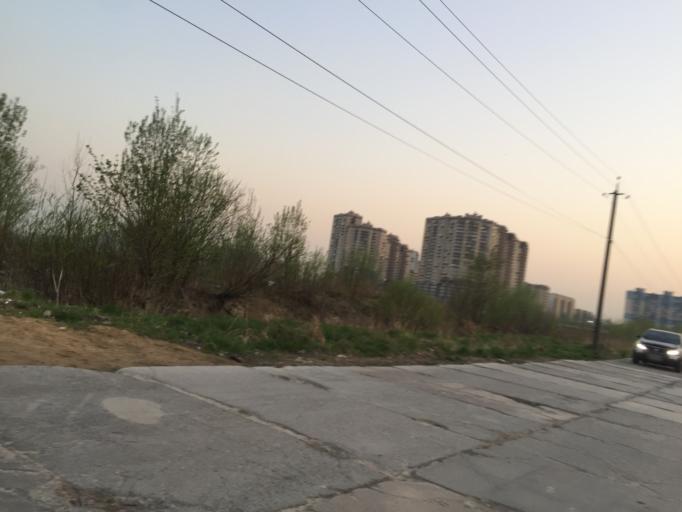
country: RU
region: Leningrad
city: Bugry
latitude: 60.0697
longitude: 30.4142
